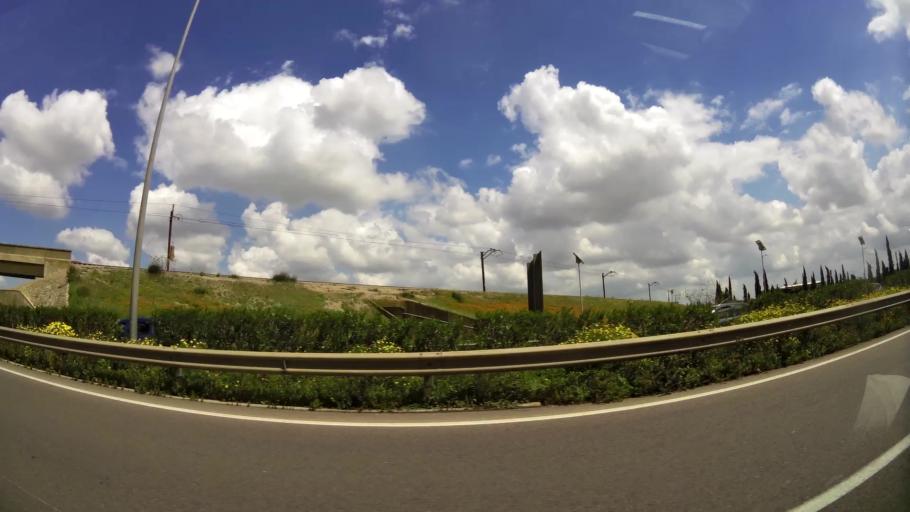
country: MA
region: Chaouia-Ouardigha
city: Nouaseur
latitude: 33.3961
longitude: -7.6207
